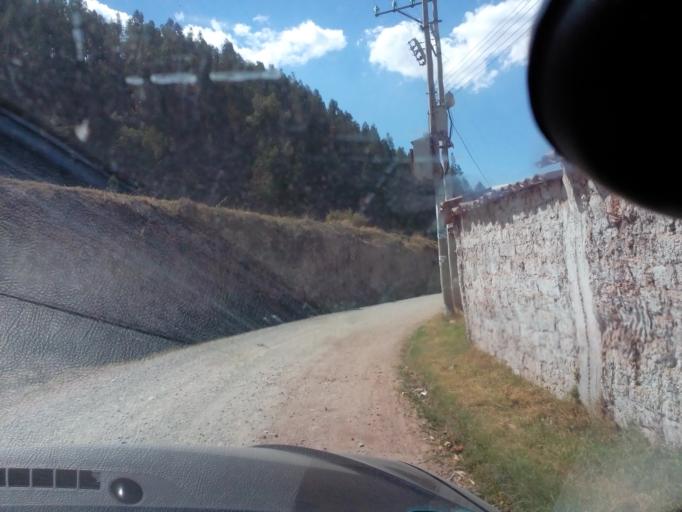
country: PE
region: Cusco
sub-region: Provincia de Anta
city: Huarocondo
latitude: -13.4340
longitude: -72.2247
